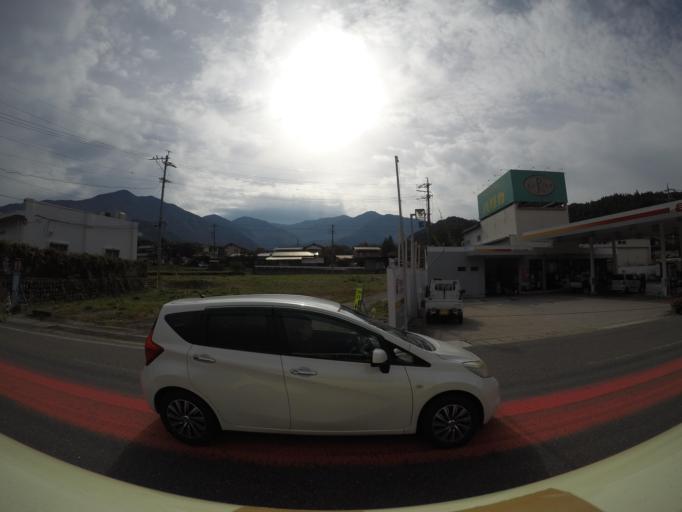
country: JP
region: Nagano
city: Ina
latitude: 35.8658
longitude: 137.7373
